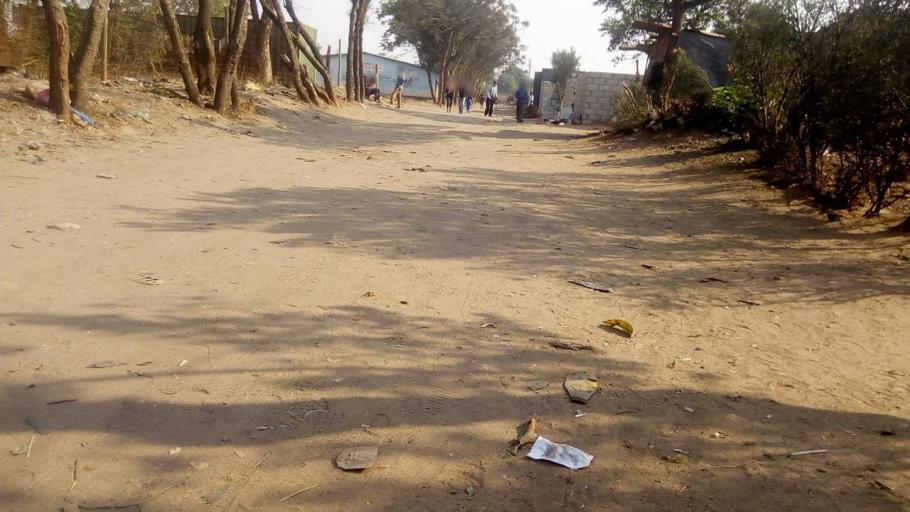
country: ZM
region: Lusaka
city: Lusaka
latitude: -15.3626
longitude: 28.2918
